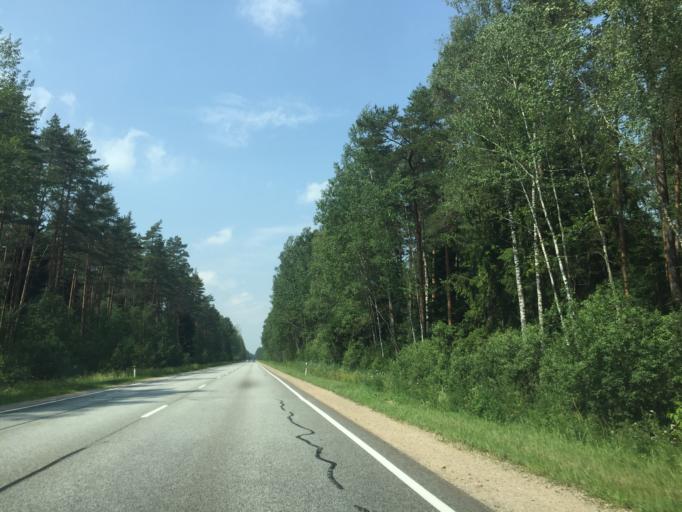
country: LV
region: Kekava
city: Balozi
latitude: 56.8166
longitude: 24.1240
